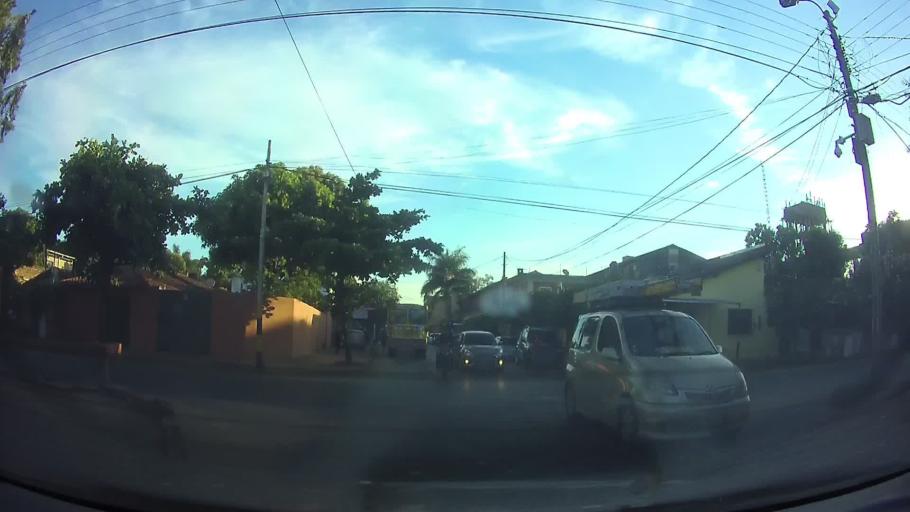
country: PY
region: Central
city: San Lorenzo
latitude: -25.2714
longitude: -57.4978
